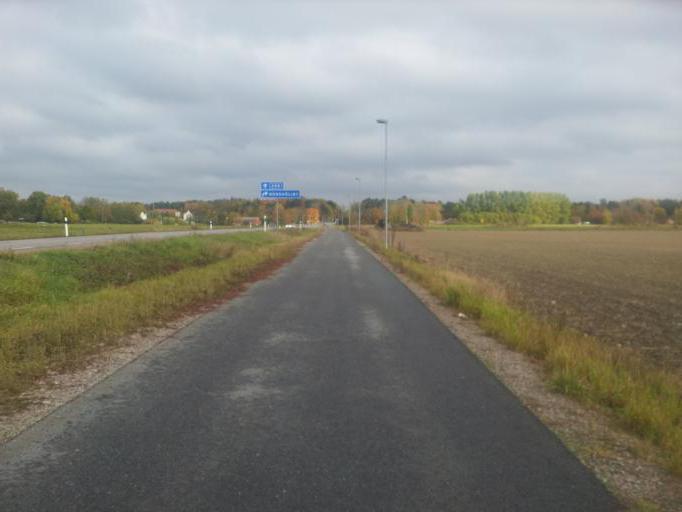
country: SE
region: Uppsala
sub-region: Uppsala Kommun
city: Storvreta
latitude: 59.8993
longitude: 17.7106
